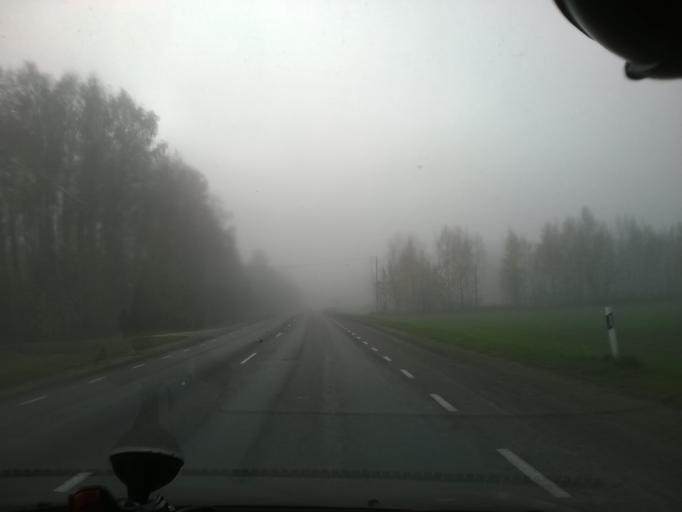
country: EE
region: Tartu
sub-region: Elva linn
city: Elva
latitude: 58.1337
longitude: 26.5216
